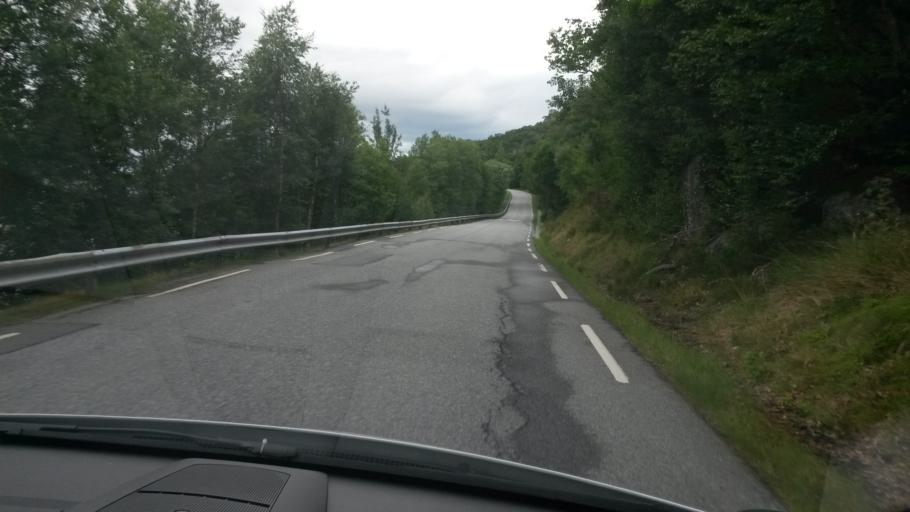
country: NO
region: Rogaland
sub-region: Sandnes
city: Sandnes
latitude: 58.8886
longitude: 5.7765
